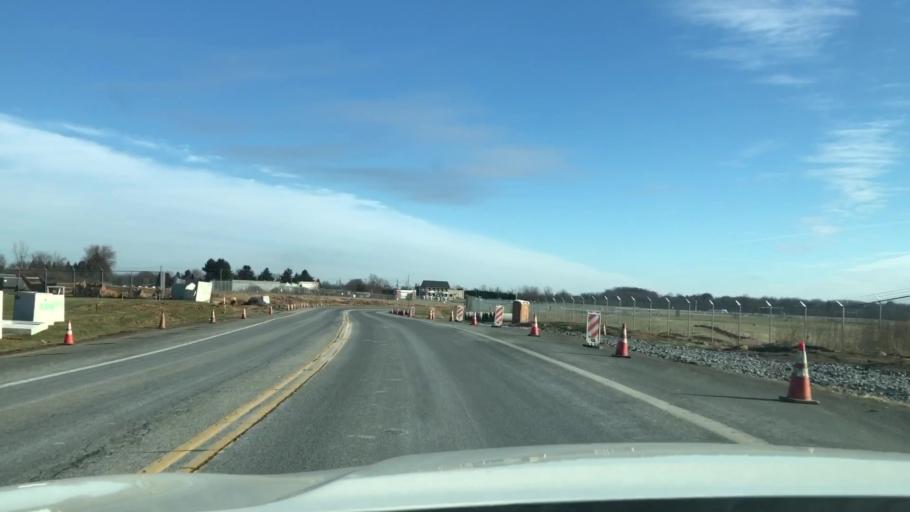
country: US
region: Pennsylvania
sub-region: Lehigh County
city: Catasauqua
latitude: 40.6619
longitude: -75.4298
